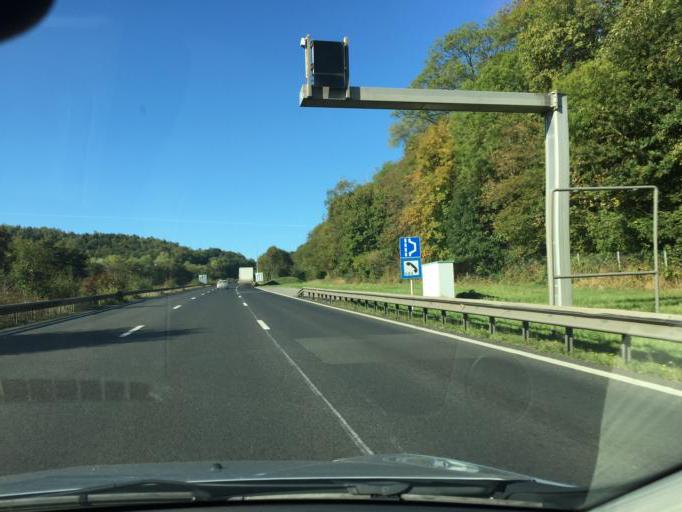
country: LU
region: Luxembourg
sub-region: Canton de Luxembourg
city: Niederanven
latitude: 49.6378
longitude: 6.2514
